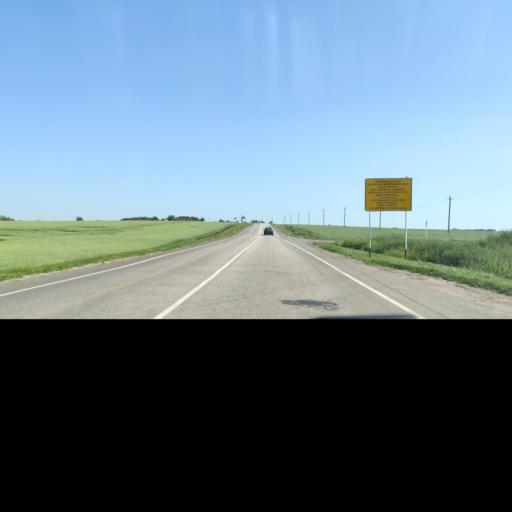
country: RU
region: Voronezj
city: Verkhnyaya Khava
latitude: 51.6885
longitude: 39.9314
